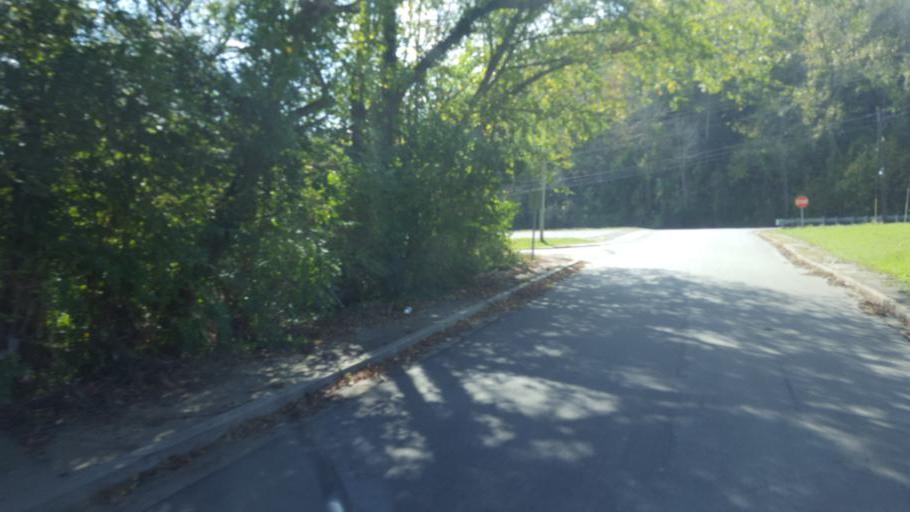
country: US
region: Ohio
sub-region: Brown County
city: Aberdeen
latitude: 38.6400
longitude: -83.7613
